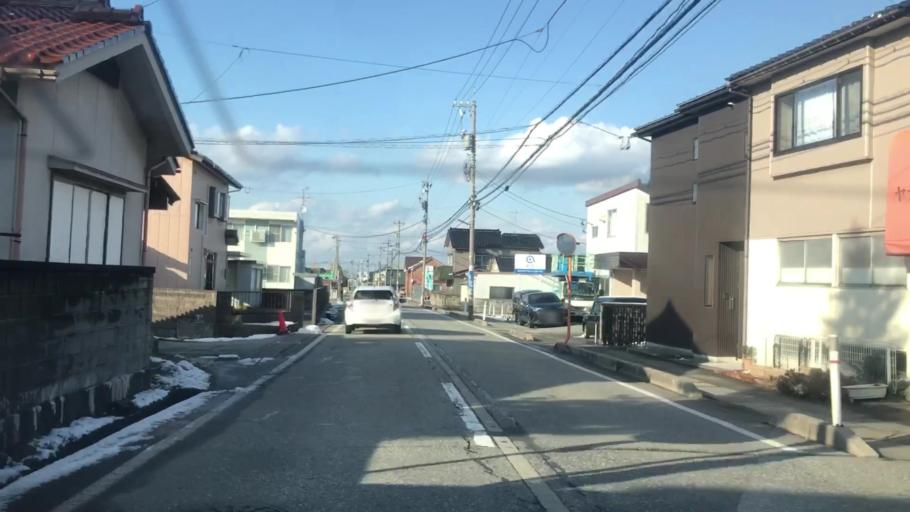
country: JP
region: Toyama
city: Toyama-shi
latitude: 36.6771
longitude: 137.2738
